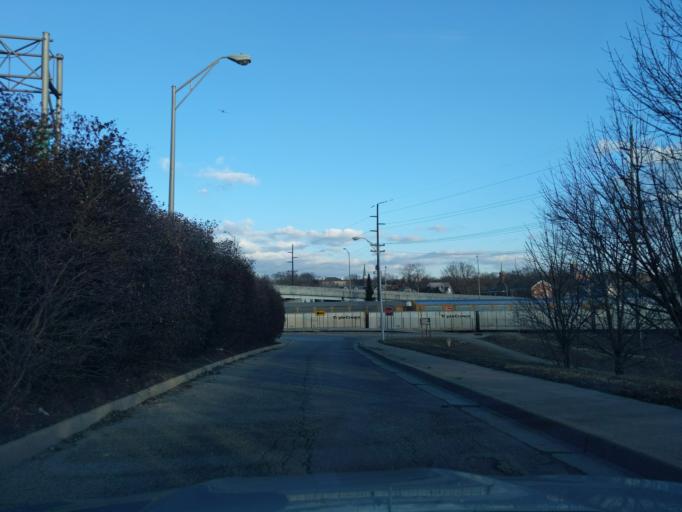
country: US
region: Indiana
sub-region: Tippecanoe County
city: West Lafayette
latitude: 40.4250
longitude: -86.8947
